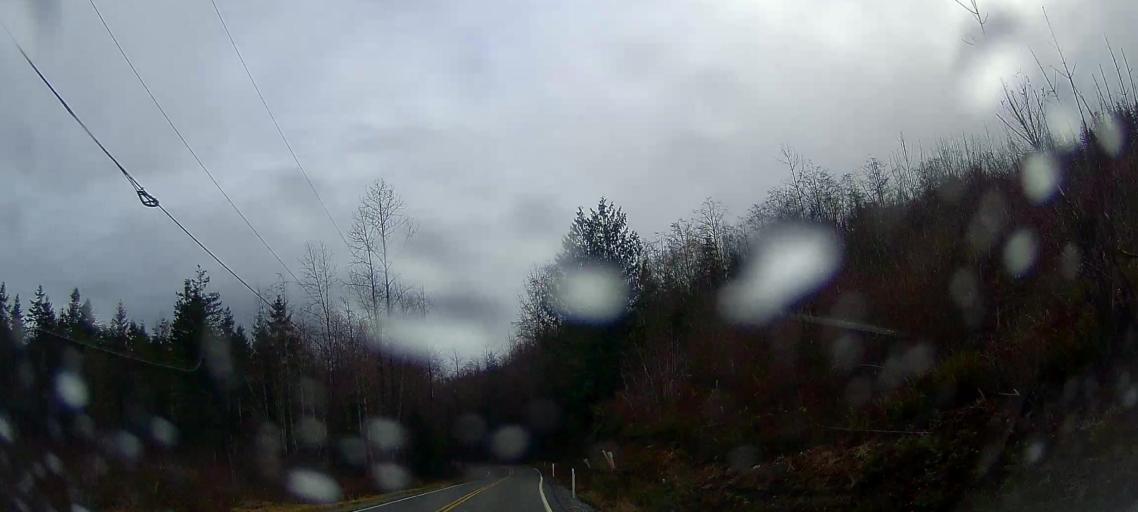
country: US
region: Washington
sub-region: Skagit County
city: Clear Lake
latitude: 48.4769
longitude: -122.1549
